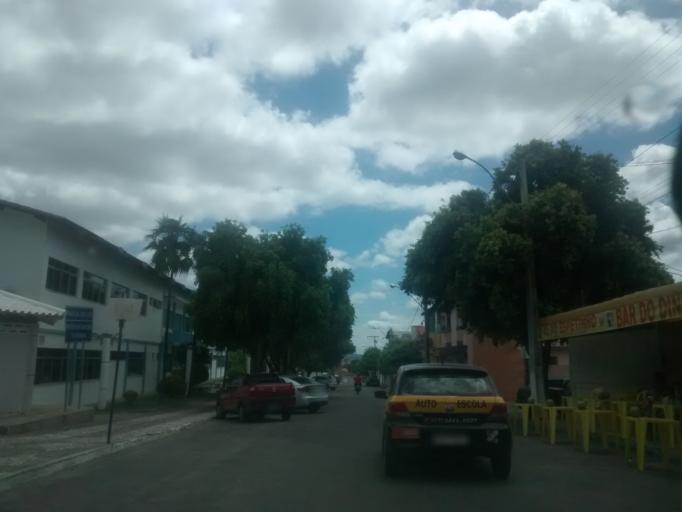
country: BR
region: Bahia
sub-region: Brumado
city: Brumado
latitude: -14.2044
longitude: -41.6702
